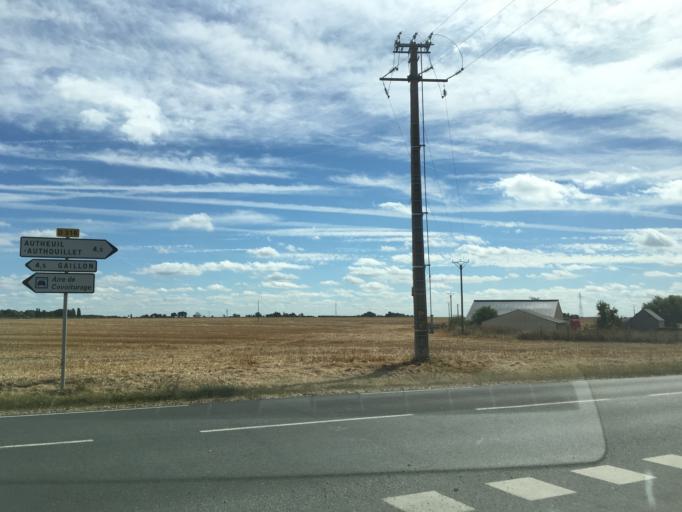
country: FR
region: Haute-Normandie
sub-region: Departement de l'Eure
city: Saint-Aubin-sur-Gaillon
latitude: 49.1306
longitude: 1.3104
